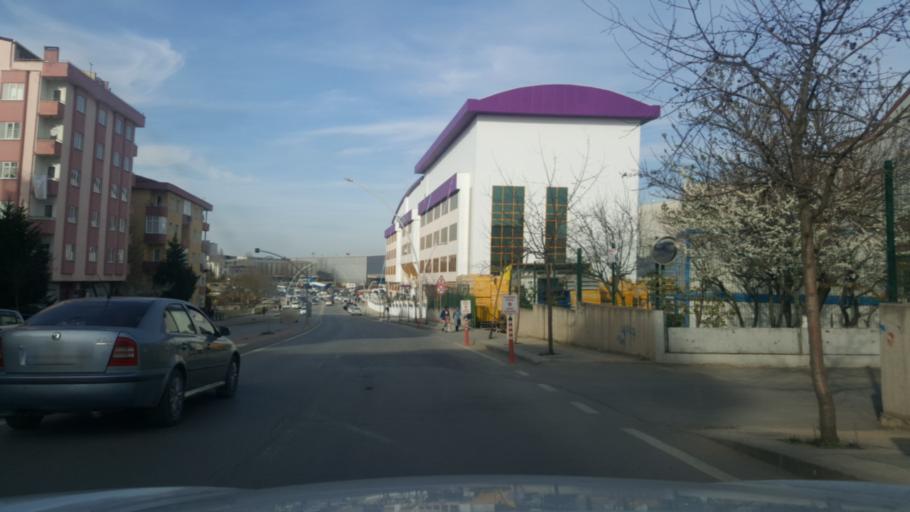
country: TR
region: Kocaeli
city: Gebze
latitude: 40.7885
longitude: 29.4415
